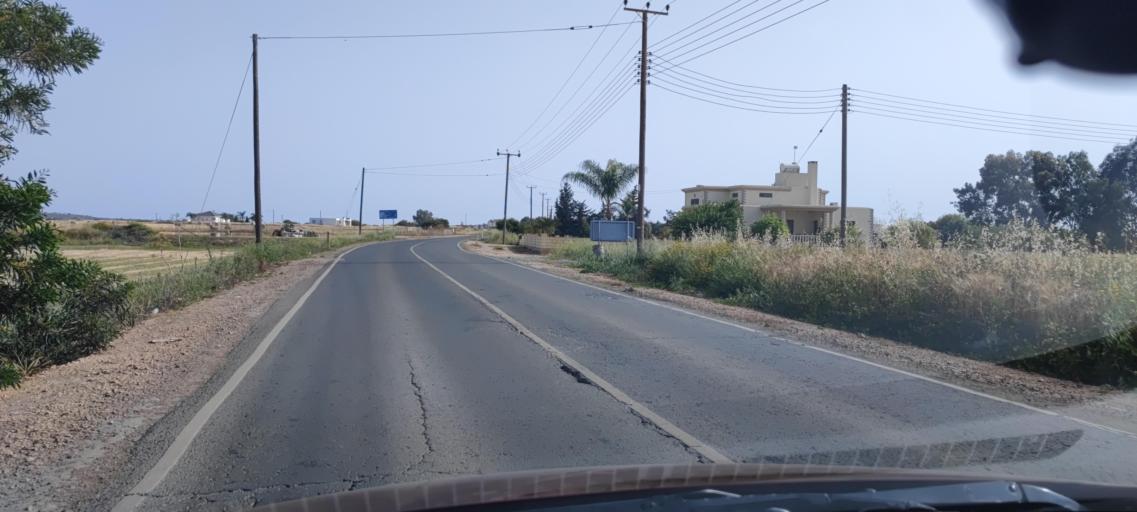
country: CY
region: Ammochostos
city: Deryneia
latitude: 35.0431
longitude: 33.9563
